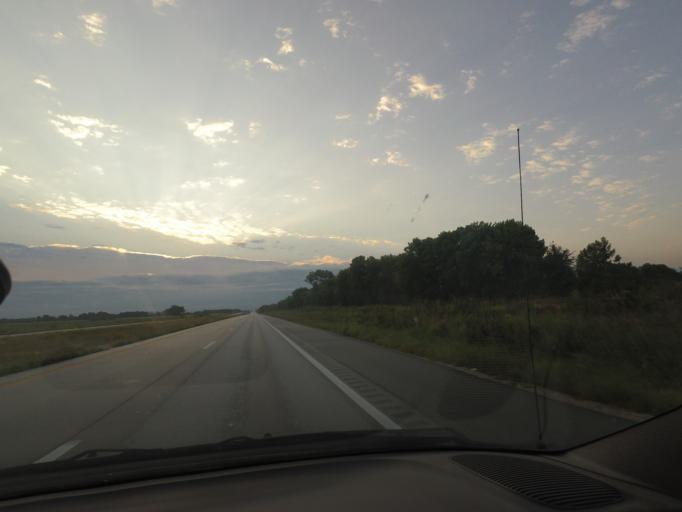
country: US
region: Missouri
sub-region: Shelby County
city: Shelbina
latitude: 39.7361
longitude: -92.2219
